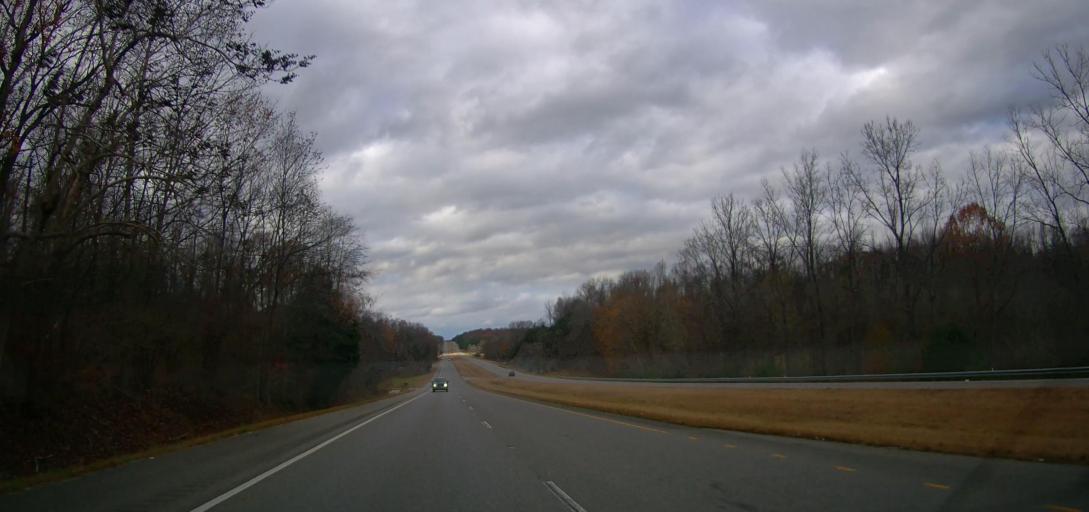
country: US
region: Alabama
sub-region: Lawrence County
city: Town Creek
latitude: 34.6041
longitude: -87.4492
